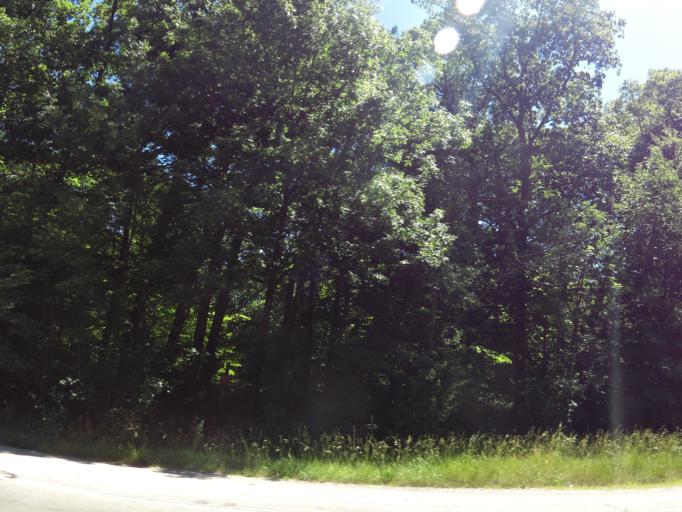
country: US
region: Illinois
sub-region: Vermilion County
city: Danville
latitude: 40.2053
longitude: -87.6325
